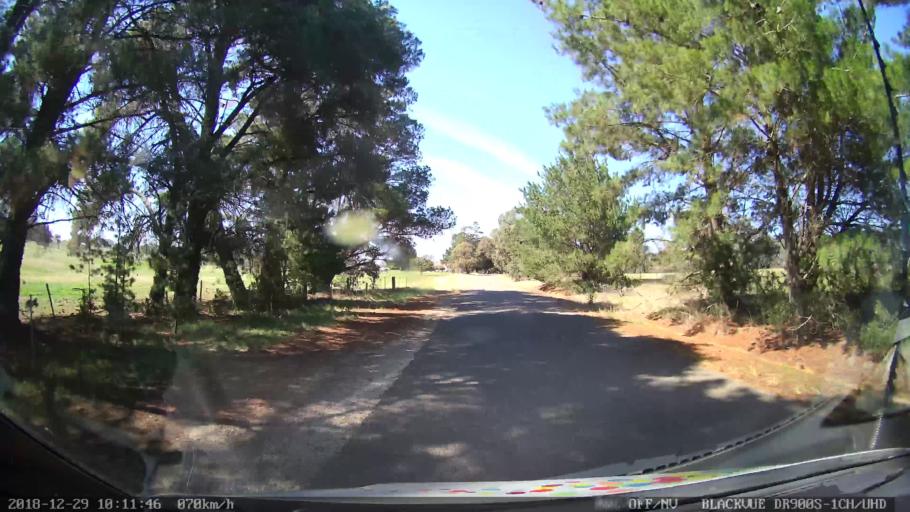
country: AU
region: New South Wales
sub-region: Yass Valley
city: Gundaroo
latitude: -34.8872
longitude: 149.4511
